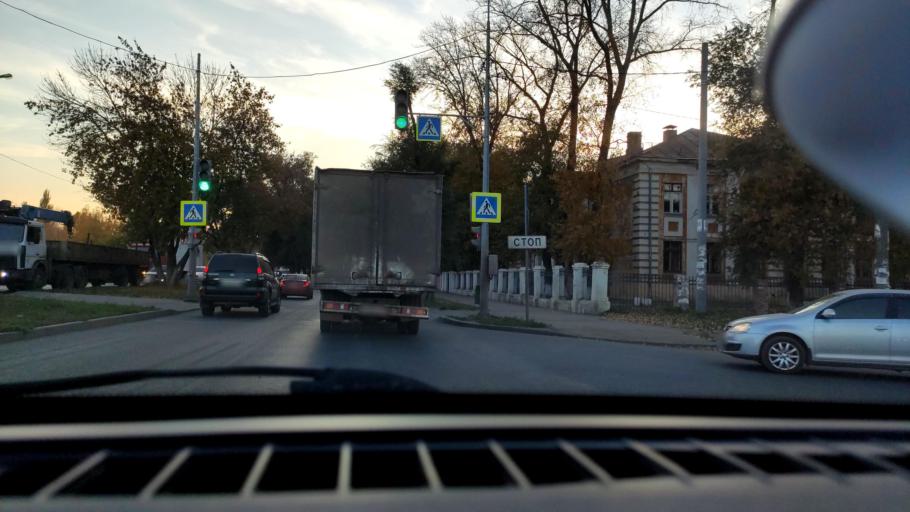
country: RU
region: Samara
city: Smyshlyayevka
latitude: 53.2133
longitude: 50.2909
